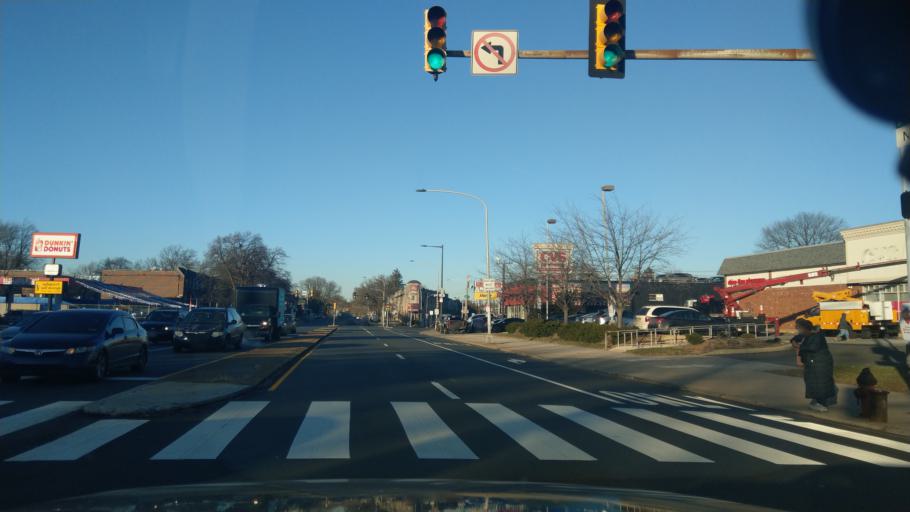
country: US
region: Pennsylvania
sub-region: Montgomery County
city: Wyncote
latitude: 40.0536
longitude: -75.1415
